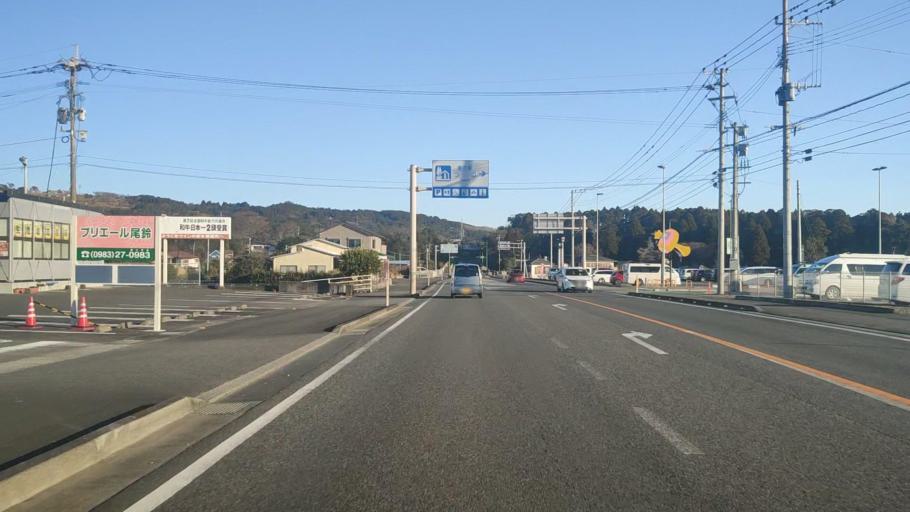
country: JP
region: Miyazaki
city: Takanabe
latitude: 32.2596
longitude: 131.5568
